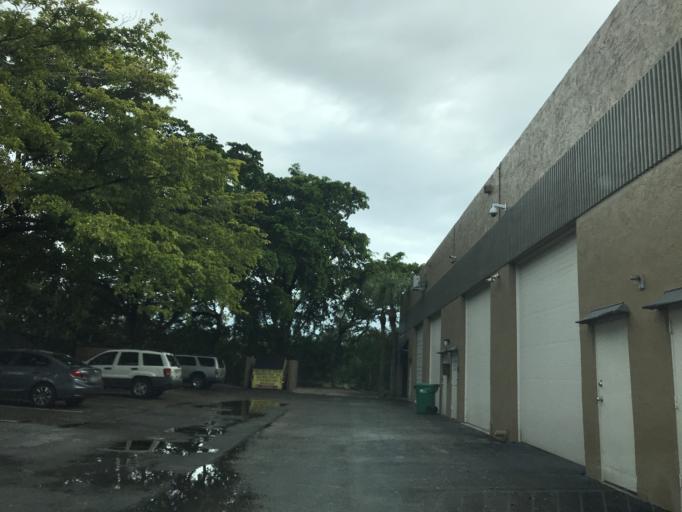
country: US
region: Florida
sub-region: Palm Beach County
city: Delray Beach
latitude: 26.4584
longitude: -80.0922
